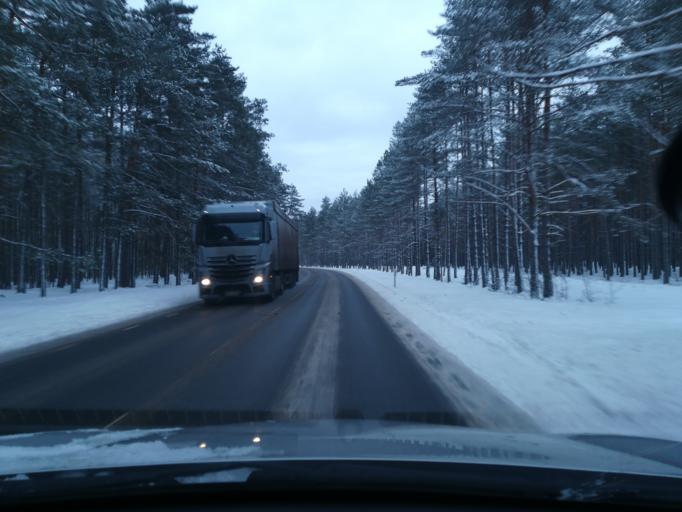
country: EE
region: Harju
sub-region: Paldiski linn
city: Paldiski
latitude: 59.3882
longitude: 24.2398
